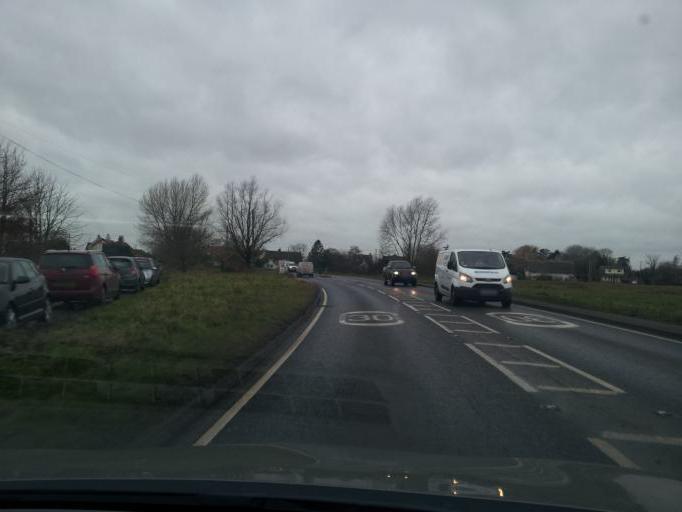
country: GB
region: England
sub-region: Suffolk
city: Botesdale
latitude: 52.3528
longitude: 1.0573
